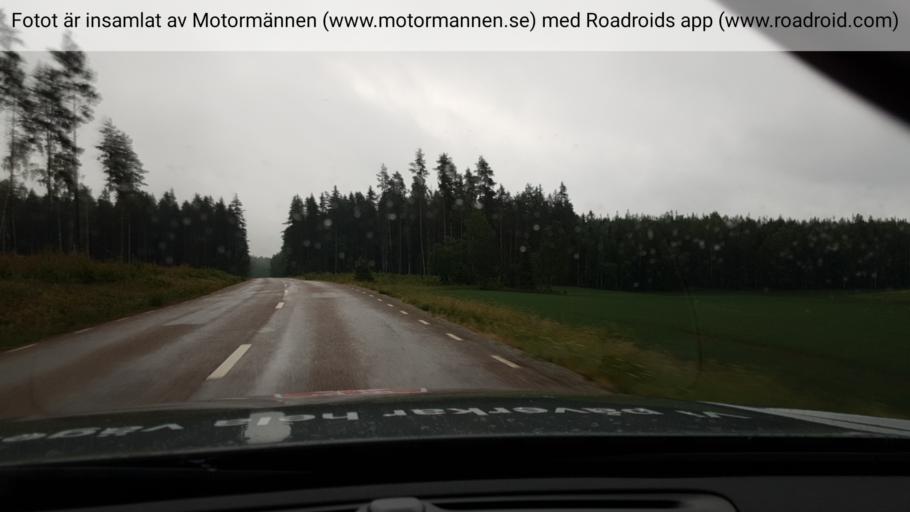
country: SE
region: Dalarna
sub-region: Avesta Kommun
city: Avesta
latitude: 59.9820
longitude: 16.1270
